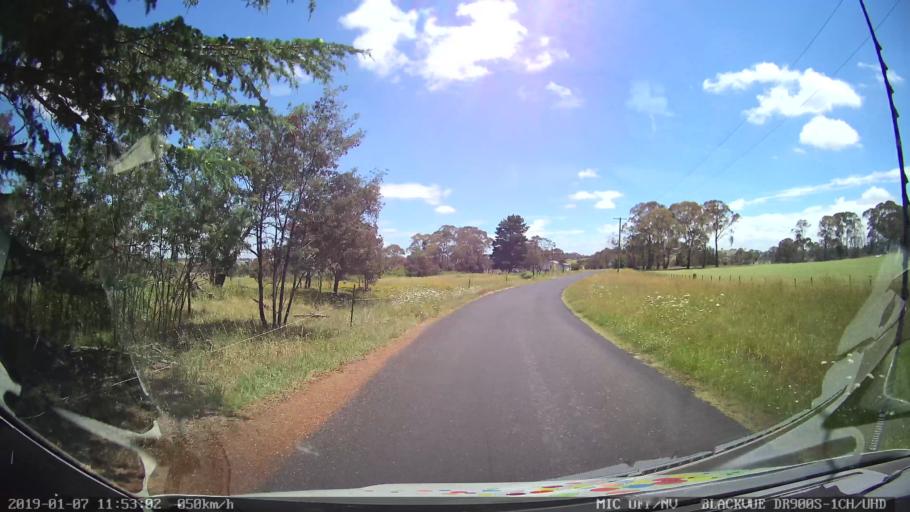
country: AU
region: New South Wales
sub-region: Guyra
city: Guyra
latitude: -30.3075
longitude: 151.6562
